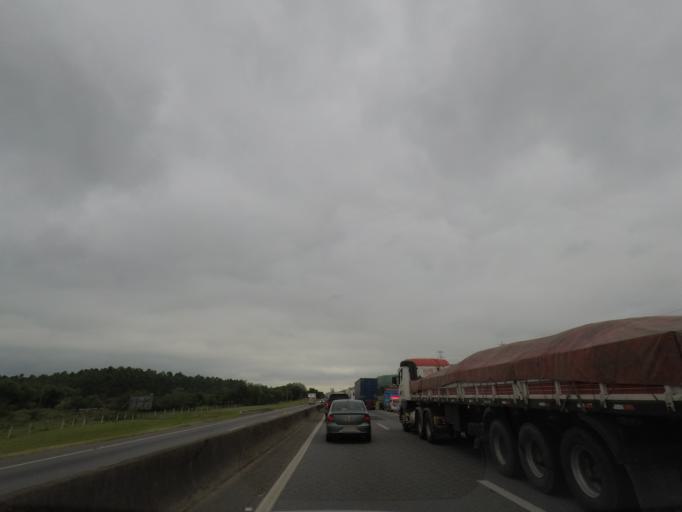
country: BR
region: Sao Paulo
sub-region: Aparecida
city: Aparecida
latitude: -22.8946
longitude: -45.2953
